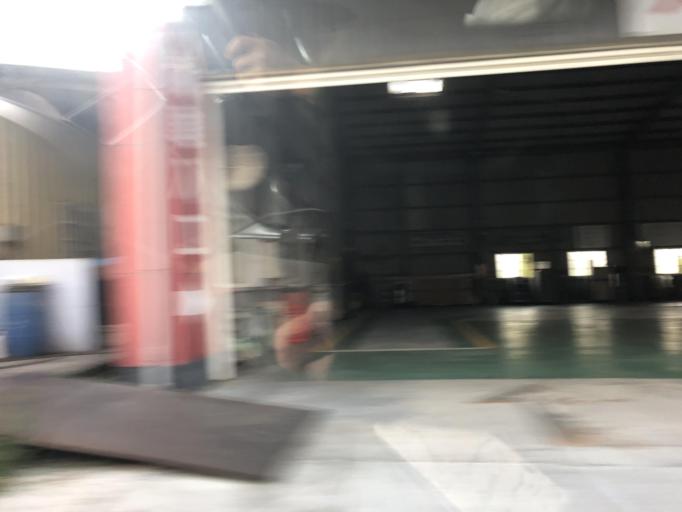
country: TW
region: Taiwan
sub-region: Tainan
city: Tainan
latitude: 23.0429
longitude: 120.2474
